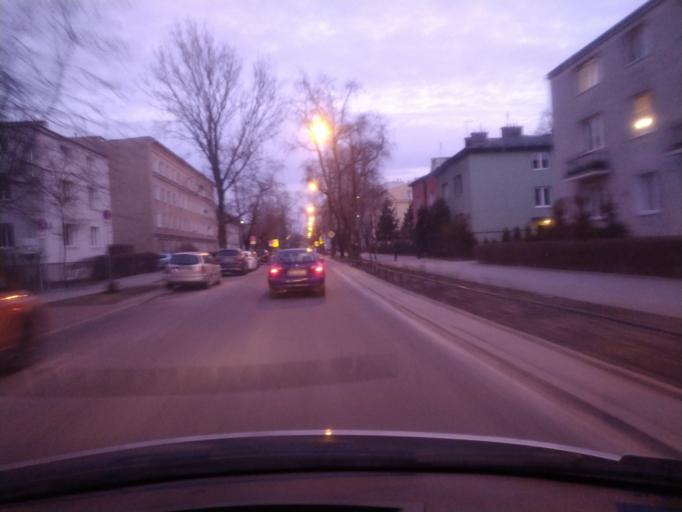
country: PL
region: Masovian Voivodeship
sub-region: Warszawa
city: Praga Poludnie
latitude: 52.2418
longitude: 21.0772
